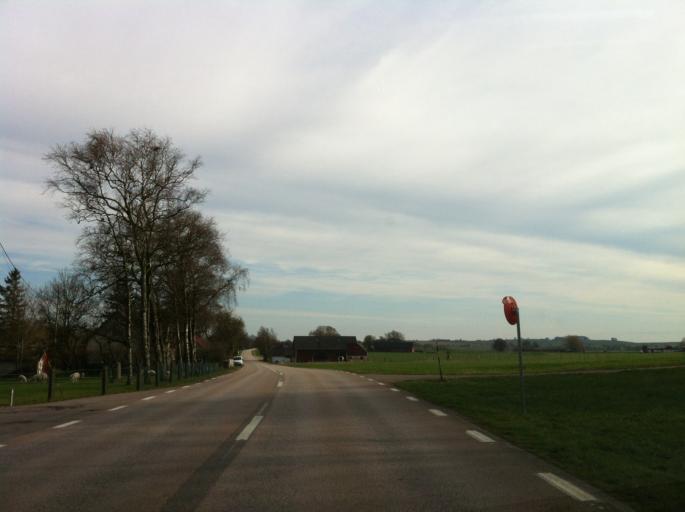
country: SE
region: Skane
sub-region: Landskrona
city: Asmundtorp
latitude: 55.9581
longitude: 12.9457
